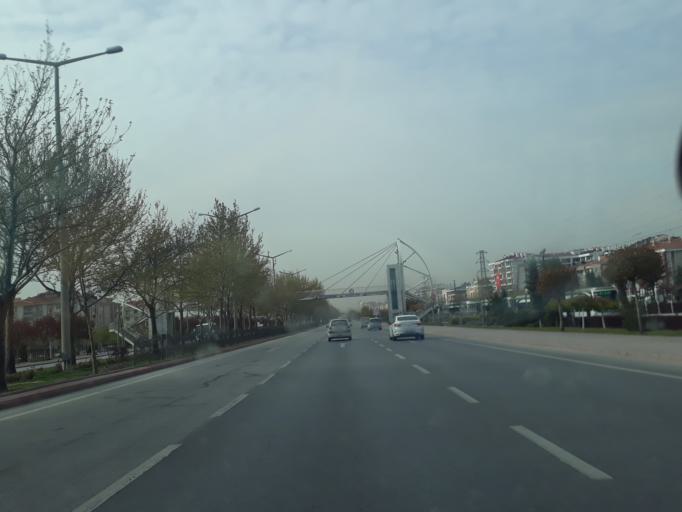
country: TR
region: Konya
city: Selcuklu
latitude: 37.9778
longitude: 32.5166
